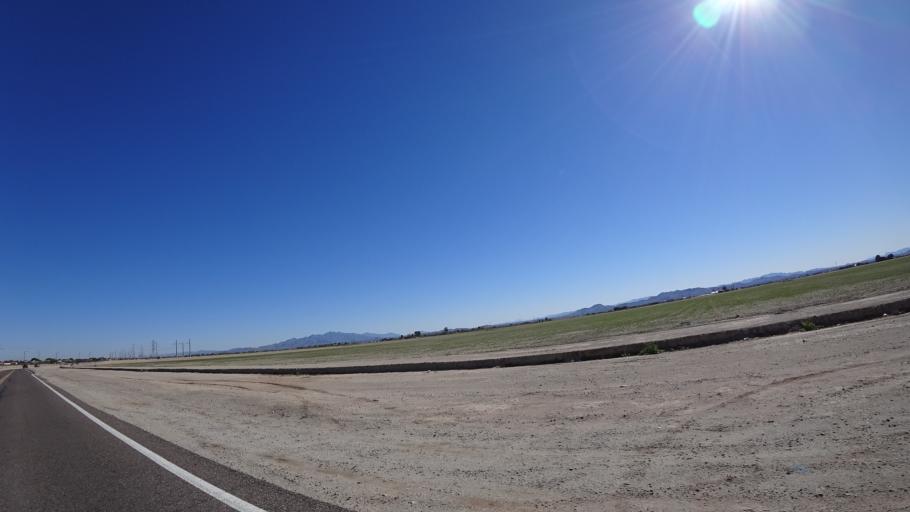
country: US
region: Arizona
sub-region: Maricopa County
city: Buckeye
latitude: 33.4220
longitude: -112.5647
